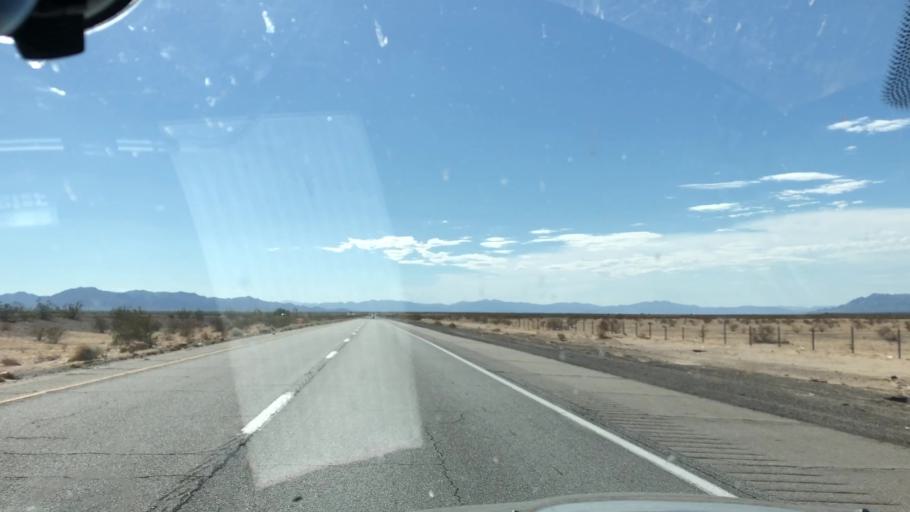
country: US
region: California
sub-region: Riverside County
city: Mesa Verde
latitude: 33.6396
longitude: -115.0949
